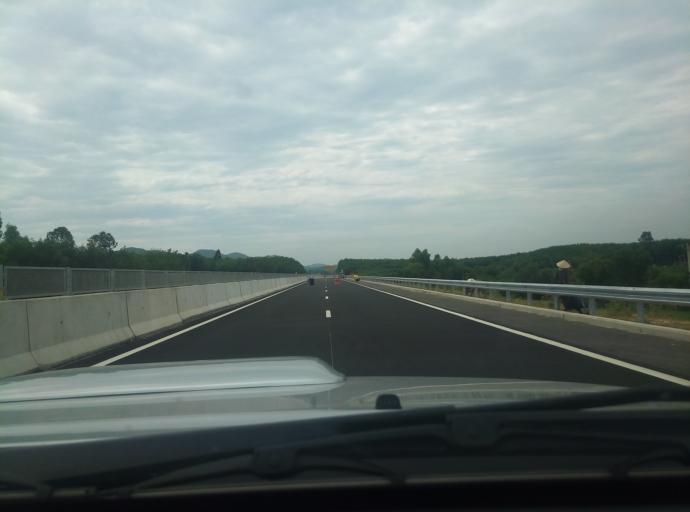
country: VN
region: Quang Nam
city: Nui Thanh
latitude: 15.4495
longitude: 108.5787
